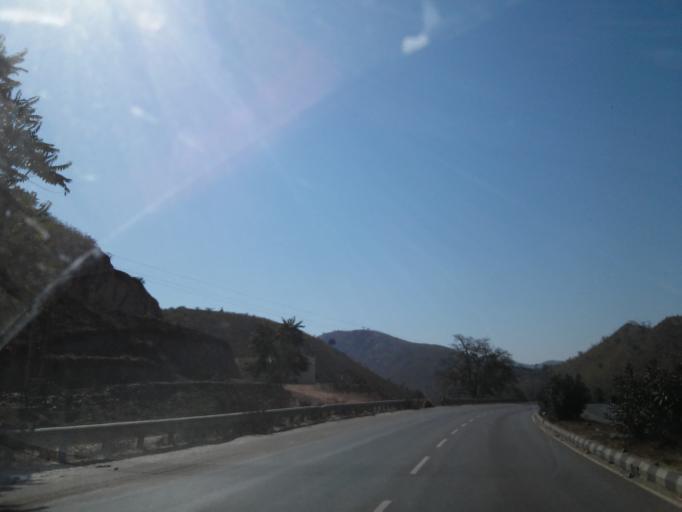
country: IN
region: Rajasthan
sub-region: Dungarpur
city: Dungarpur
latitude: 24.1918
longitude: 73.6996
